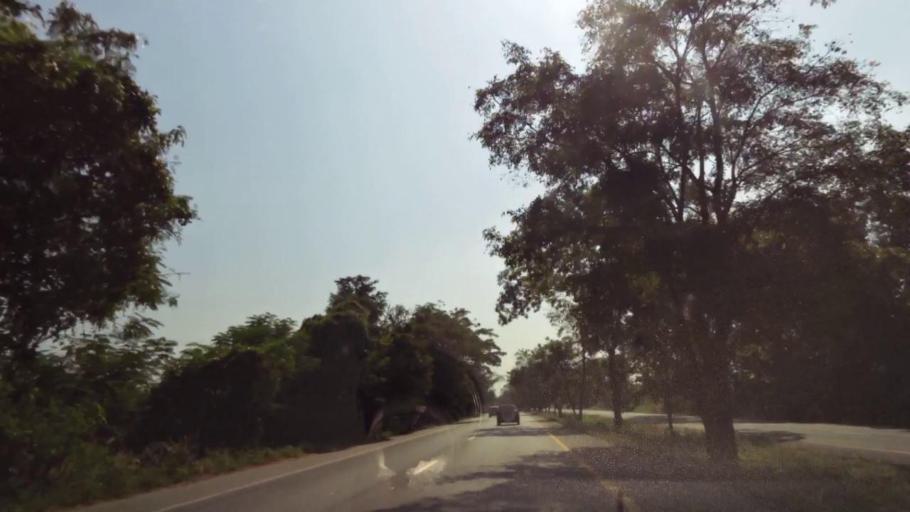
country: TH
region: Phichit
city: Bueng Na Rang
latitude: 16.0219
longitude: 100.1146
